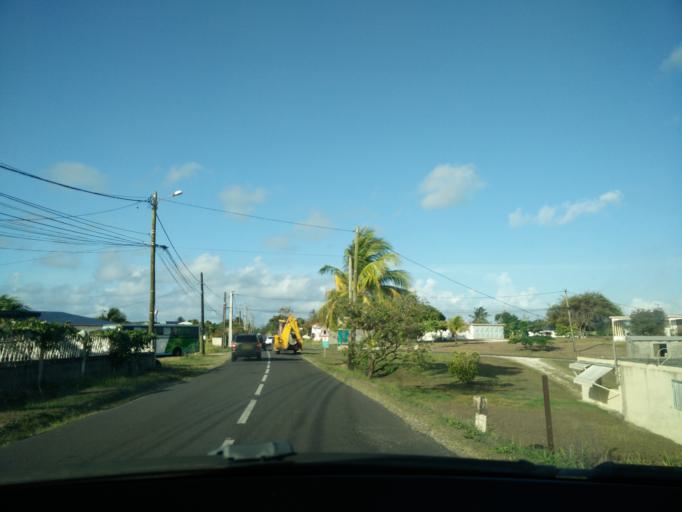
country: GP
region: Guadeloupe
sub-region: Guadeloupe
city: Sainte-Anne
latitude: 16.2816
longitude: -61.3742
